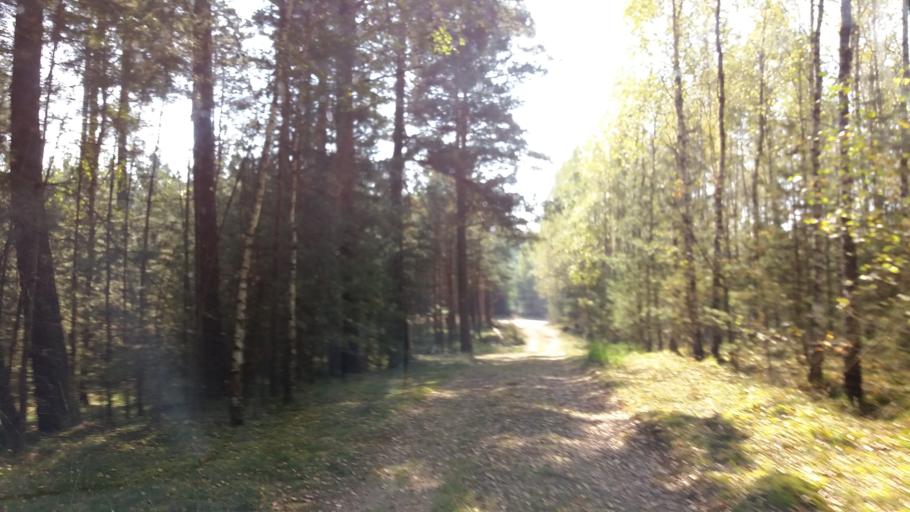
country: PL
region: West Pomeranian Voivodeship
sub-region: Powiat drawski
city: Kalisz Pomorski
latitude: 53.1189
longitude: 15.9355
